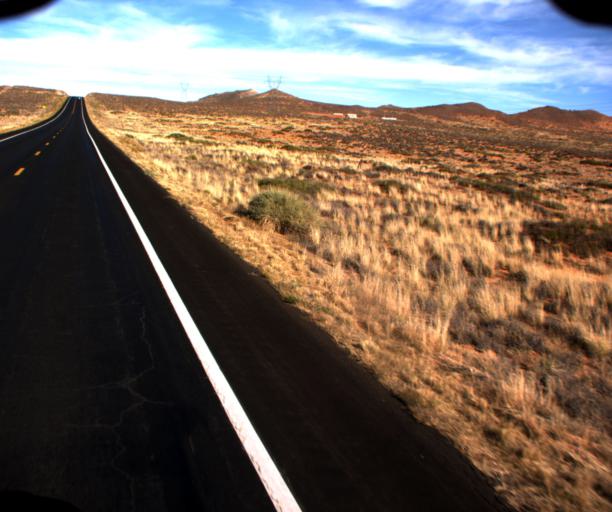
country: US
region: Arizona
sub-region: Apache County
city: Many Farms
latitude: 36.9492
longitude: -109.5219
